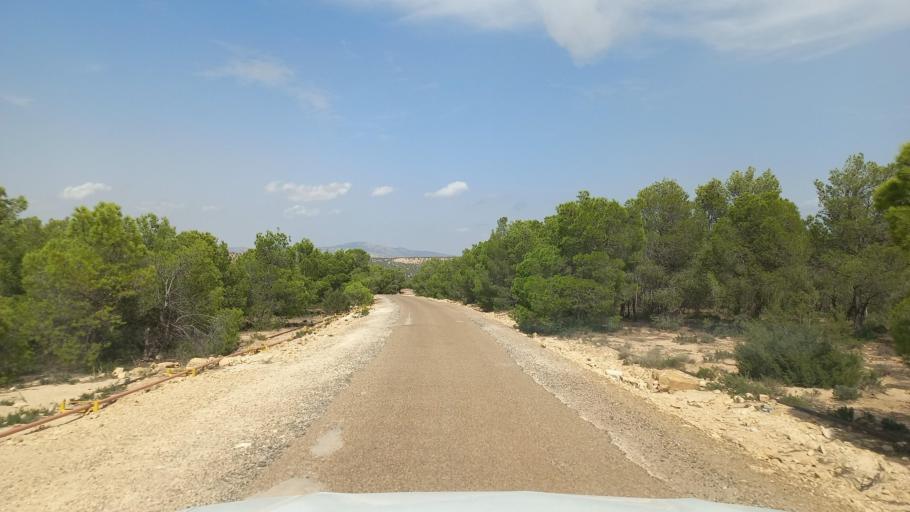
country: TN
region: Al Qasrayn
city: Sbiba
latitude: 35.3910
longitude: 8.9091
